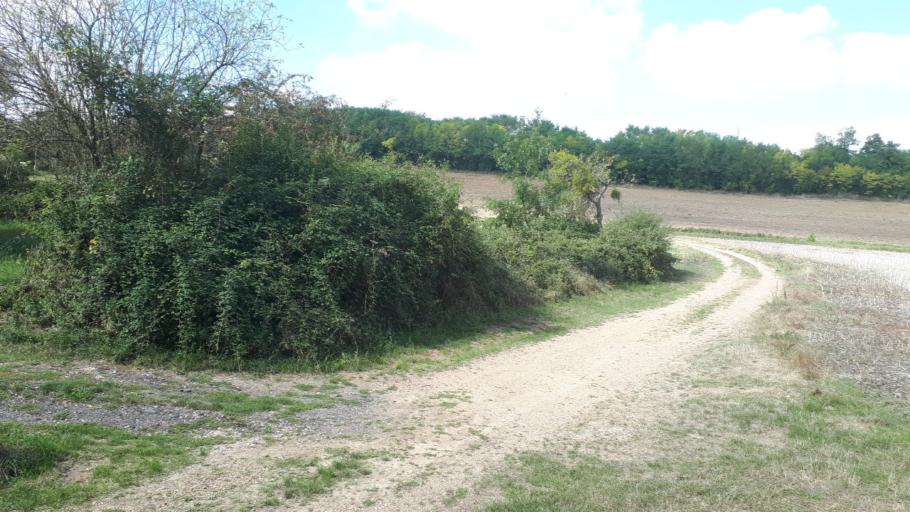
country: FR
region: Centre
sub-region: Departement du Loir-et-Cher
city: Villiers-sur-Loir
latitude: 47.8226
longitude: 0.9675
